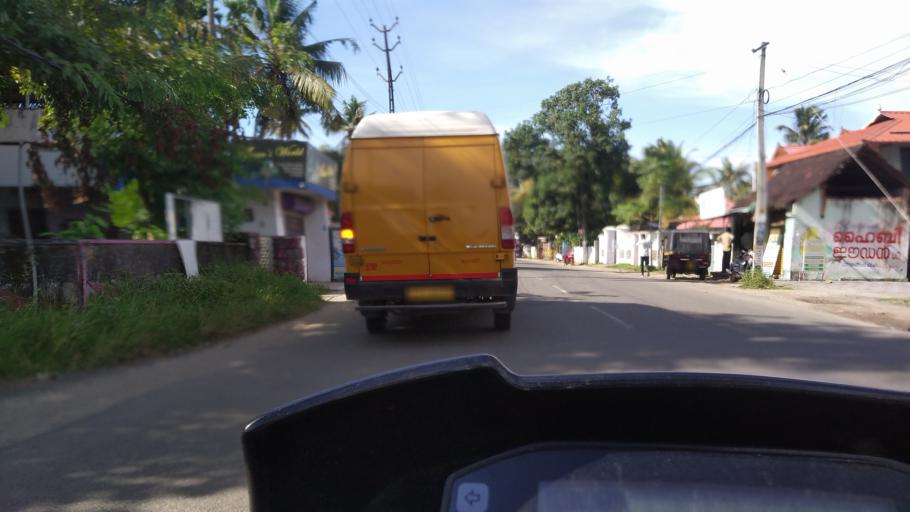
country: IN
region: Kerala
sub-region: Ernakulam
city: Elur
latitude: 10.0348
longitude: 76.2207
